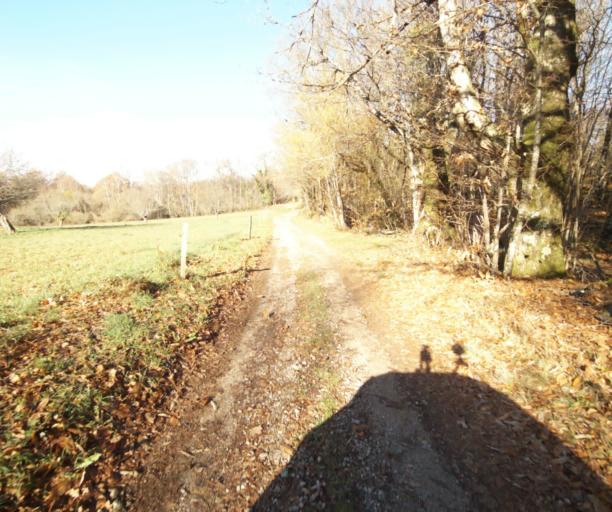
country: FR
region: Limousin
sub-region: Departement de la Correze
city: Sainte-Fortunade
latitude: 45.2151
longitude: 1.7791
